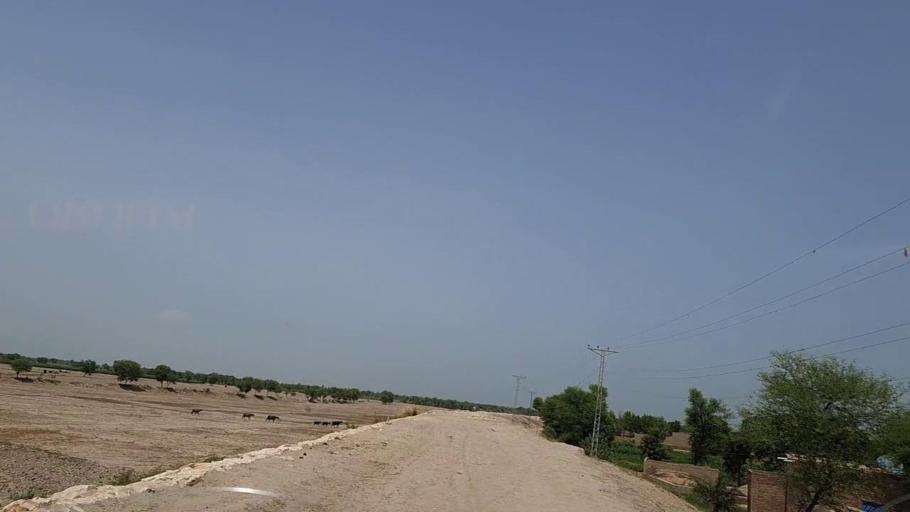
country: PK
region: Sindh
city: Tharu Shah
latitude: 27.0162
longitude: 68.1037
